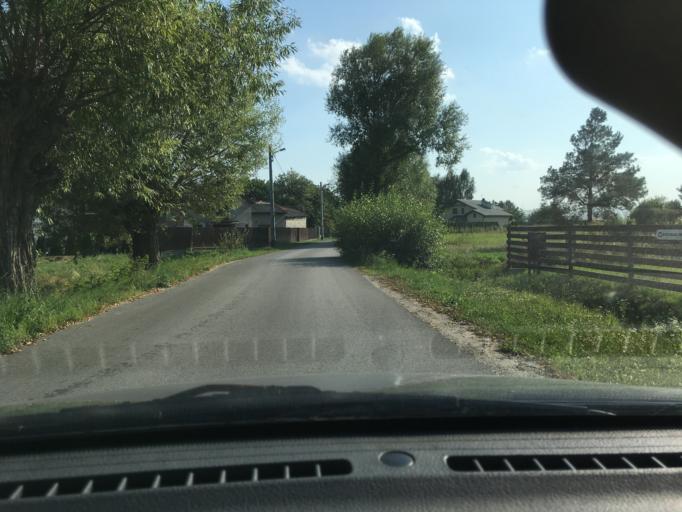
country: PL
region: Masovian Voivodeship
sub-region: Powiat piaseczynski
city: Lesznowola
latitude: 52.0510
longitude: 20.9448
